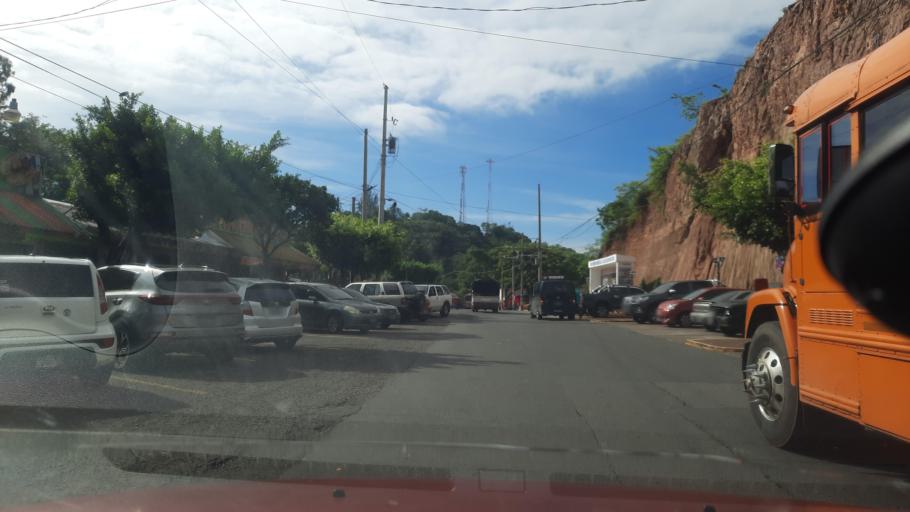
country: SV
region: La Paz
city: Olocuilta
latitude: 13.5639
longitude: -89.1172
